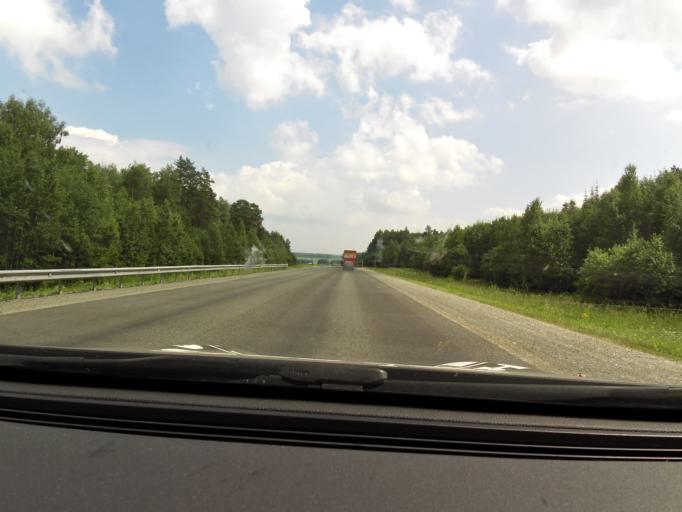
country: RU
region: Sverdlovsk
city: Achit
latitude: 56.7778
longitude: 57.9883
